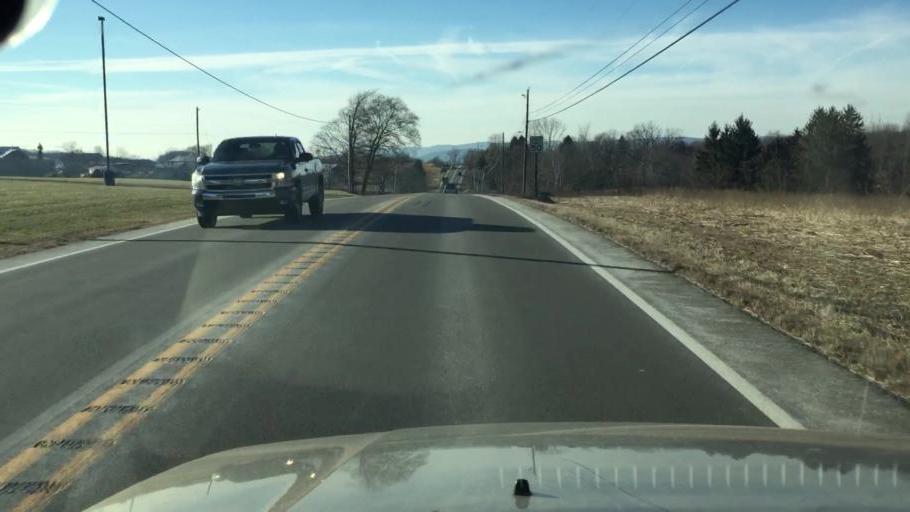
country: US
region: Pennsylvania
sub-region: Luzerne County
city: Nescopeck
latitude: 41.0510
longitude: -76.1591
